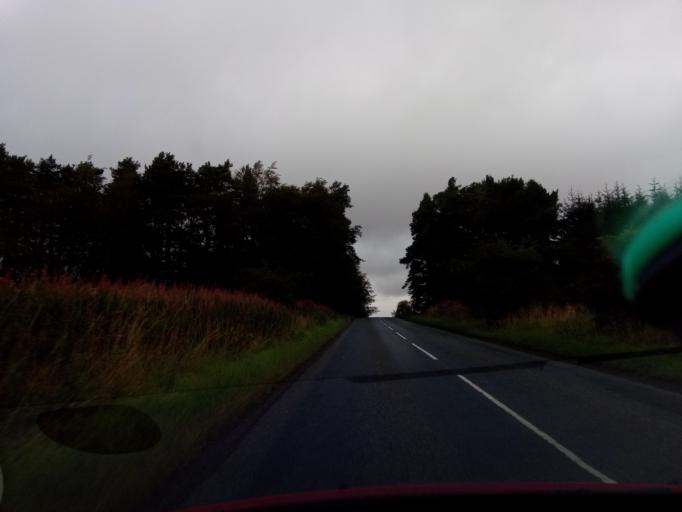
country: GB
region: Scotland
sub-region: The Scottish Borders
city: Earlston
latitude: 55.6633
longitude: -2.5519
